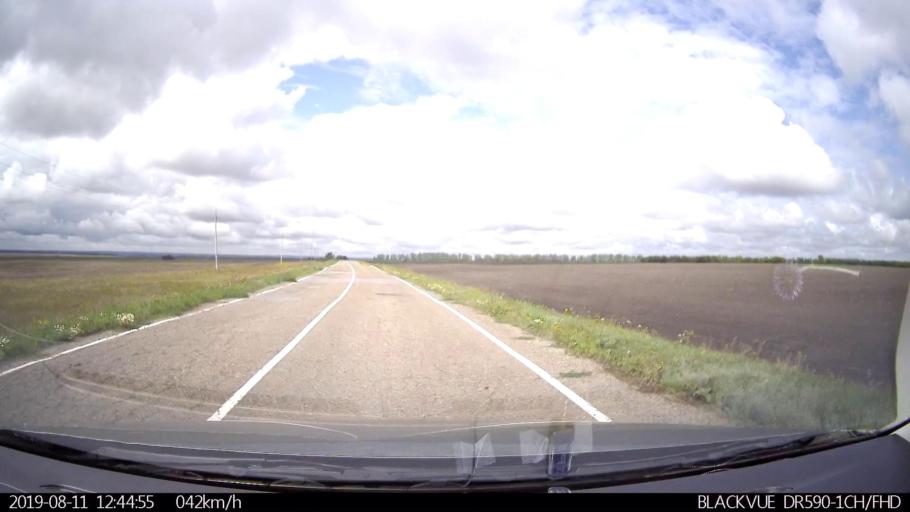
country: RU
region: Ulyanovsk
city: Ignatovka
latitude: 53.8570
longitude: 47.7326
